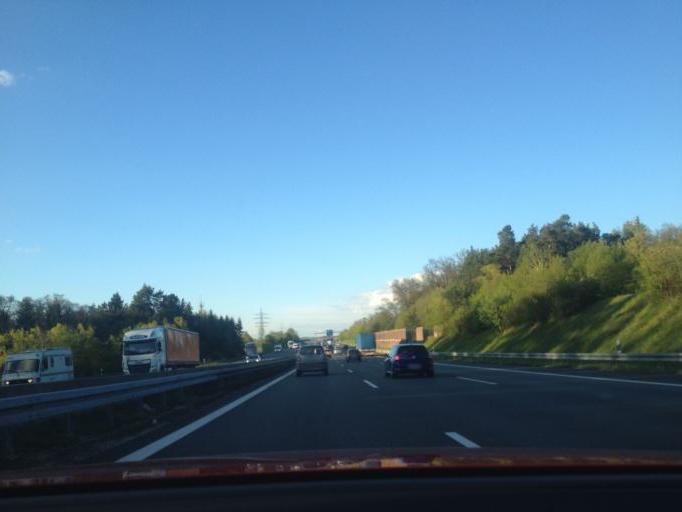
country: DE
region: Bavaria
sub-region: Regierungsbezirk Mittelfranken
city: Ruckersdorf
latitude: 49.4838
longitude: 11.2710
